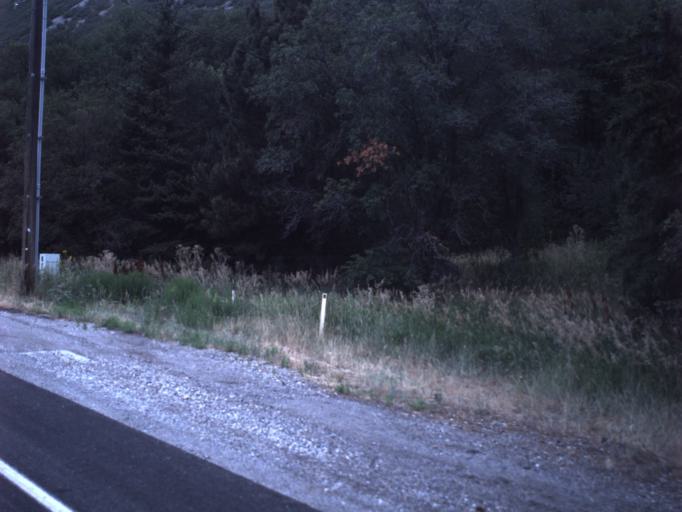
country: US
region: Utah
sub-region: Salt Lake County
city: Granite
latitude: 40.5736
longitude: -111.7782
